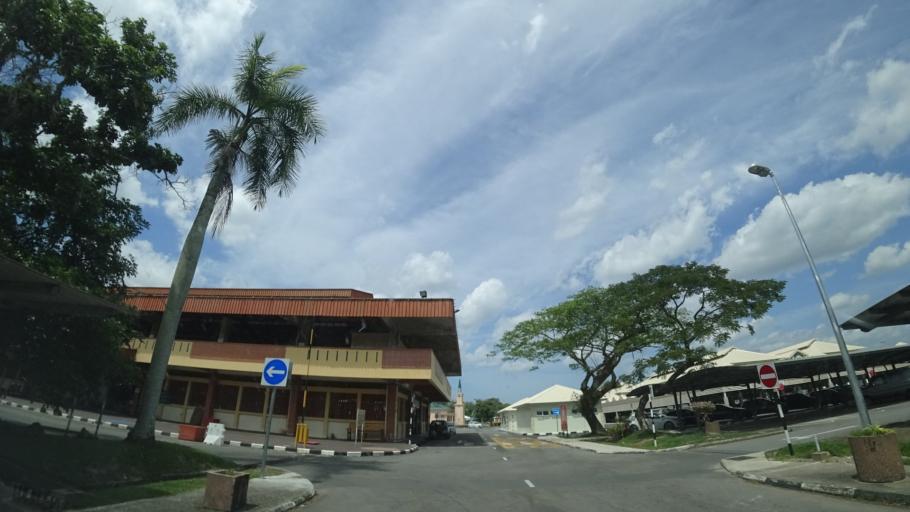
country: BN
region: Brunei and Muara
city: Bandar Seri Begawan
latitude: 4.9035
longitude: 114.9187
